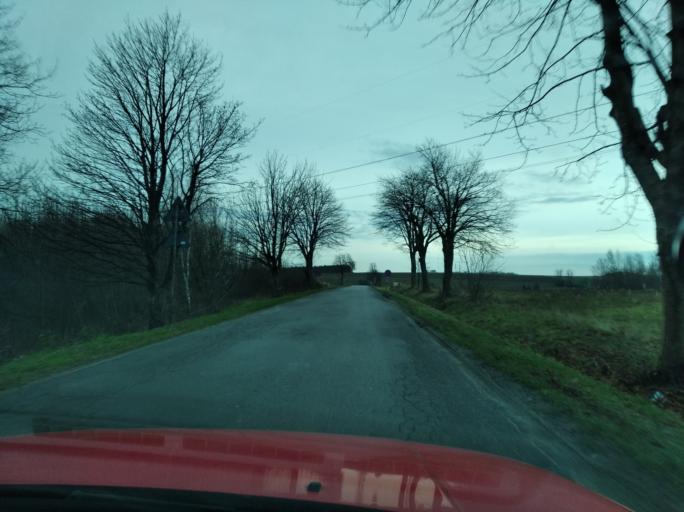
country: PL
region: Subcarpathian Voivodeship
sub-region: Powiat strzyzowski
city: Jawornik
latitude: 49.8735
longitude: 21.8572
